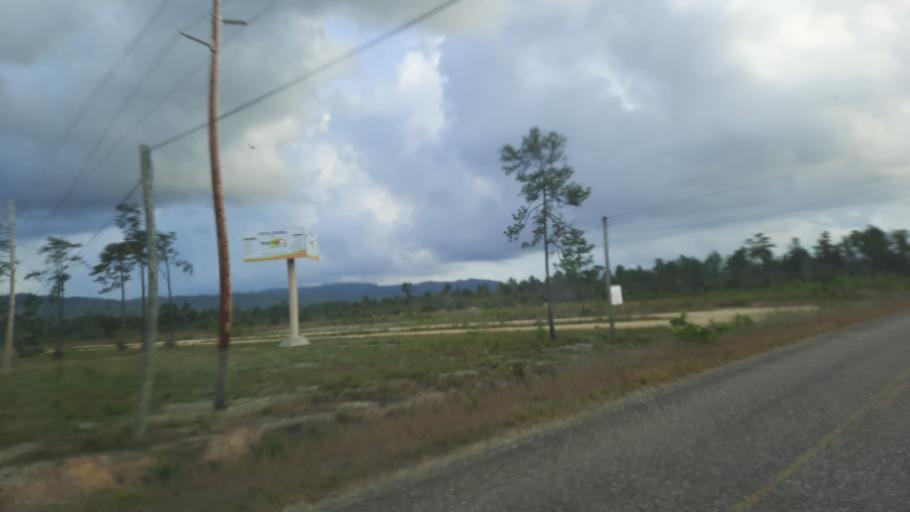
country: BZ
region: Stann Creek
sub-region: Dangriga
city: Dangriga
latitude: 16.7670
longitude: -88.3839
